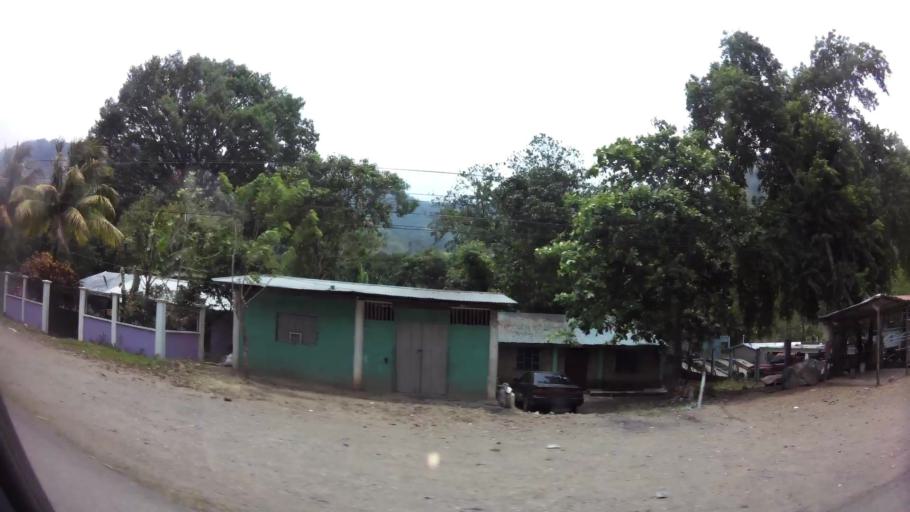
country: HN
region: Comayagua
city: Taulabe
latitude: 14.7317
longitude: -87.9639
